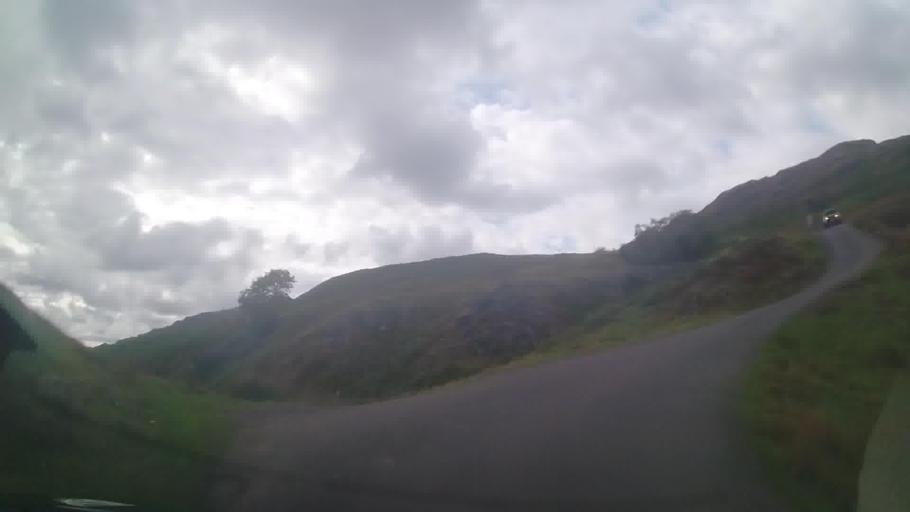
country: GB
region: England
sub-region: Cumbria
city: Keswick
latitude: 54.4042
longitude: -3.1736
